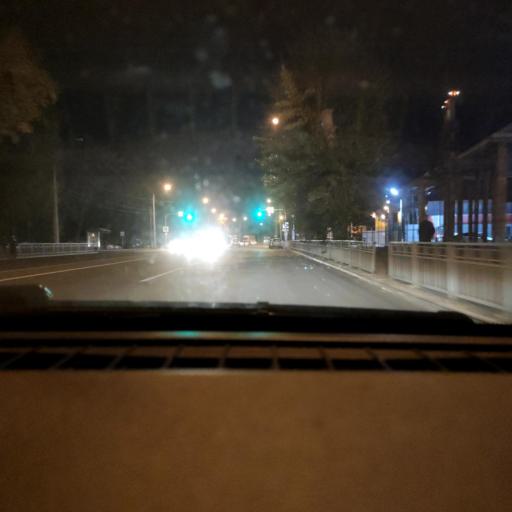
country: RU
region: Voronezj
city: Maslovka
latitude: 51.6033
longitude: 39.2439
